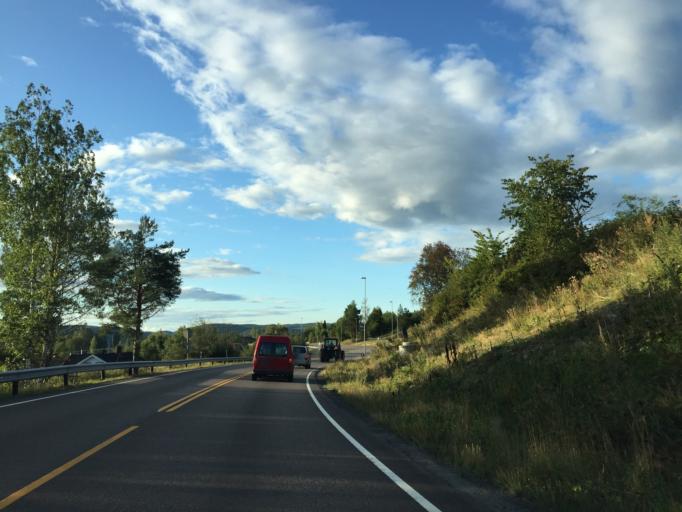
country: NO
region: Akershus
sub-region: Fet
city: Fetsund
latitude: 59.9165
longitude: 11.1841
